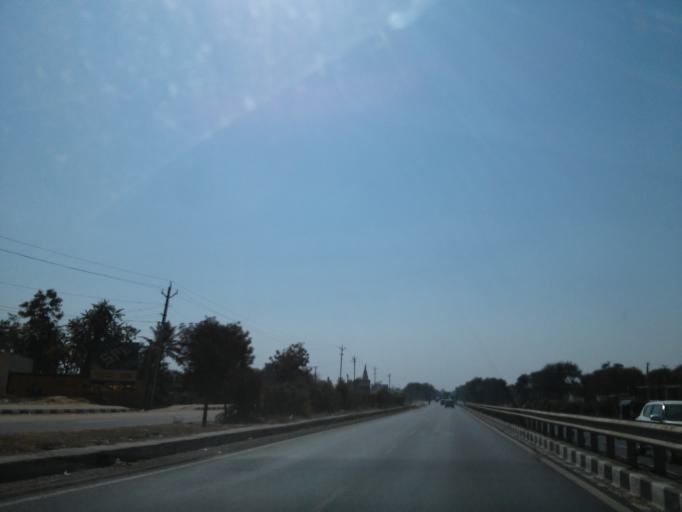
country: IN
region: Gujarat
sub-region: Gandhinagar
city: Chhala
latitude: 23.3104
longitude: 72.7742
